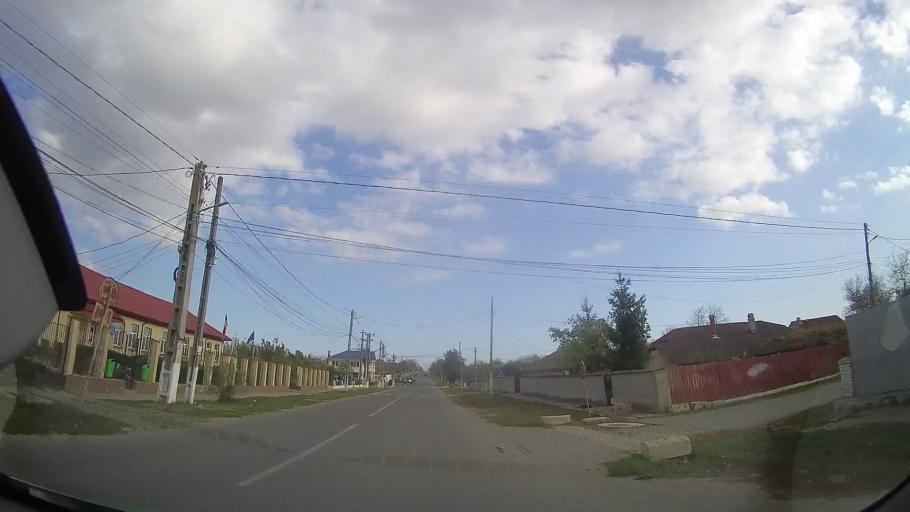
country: RO
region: Constanta
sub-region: Comuna Pecineaga
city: Pecineaga
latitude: 43.8952
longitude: 28.4980
